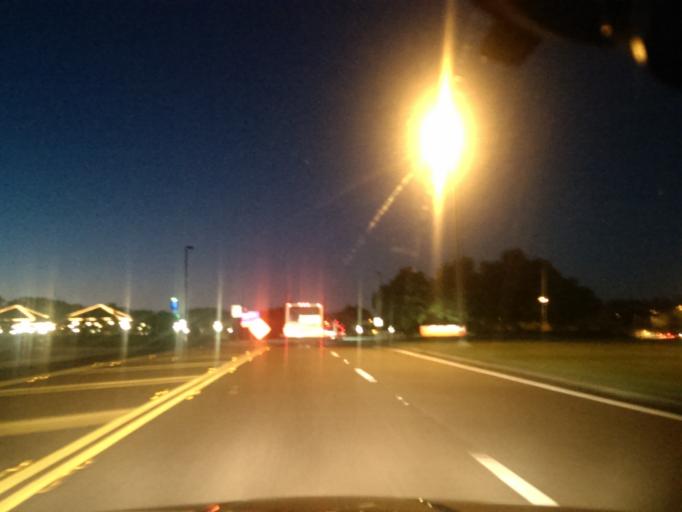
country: US
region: Florida
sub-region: Orange County
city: Bay Hill
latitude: 28.4143
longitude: -81.5765
